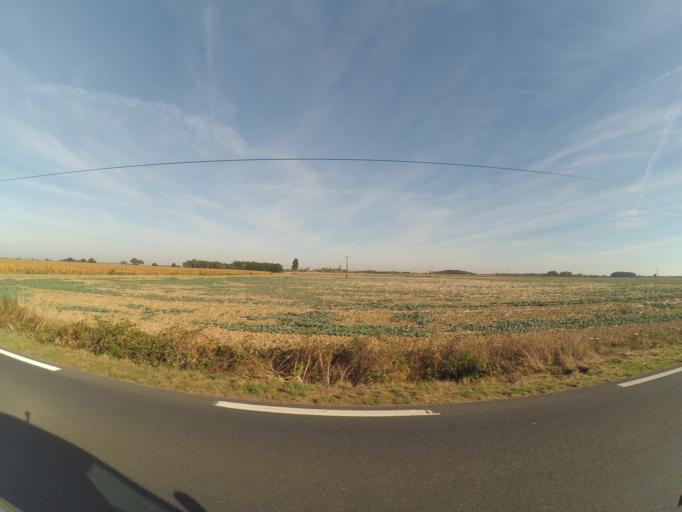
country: FR
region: Pays de la Loire
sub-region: Departement de la Vendee
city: Bouffere
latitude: 46.9728
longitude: -1.3784
